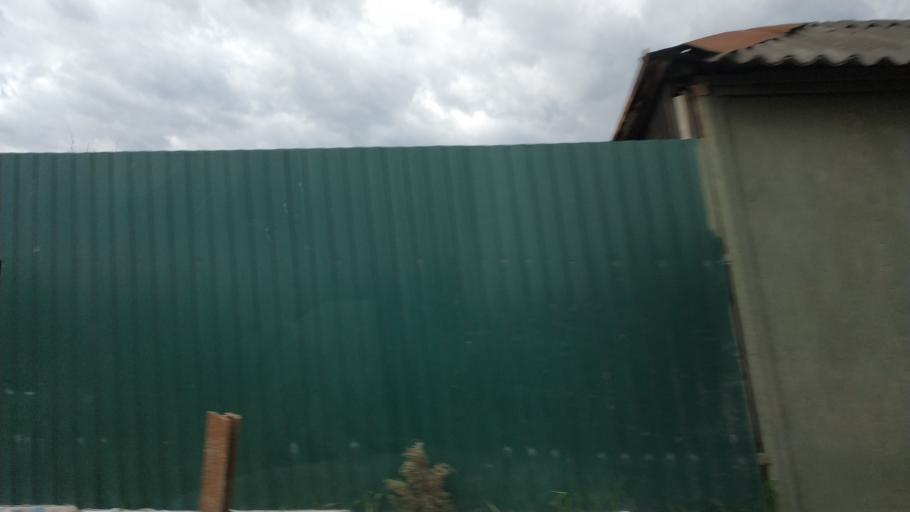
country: RU
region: Moskovskaya
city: Pavlovskiy Posad
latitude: 55.7903
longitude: 38.6849
